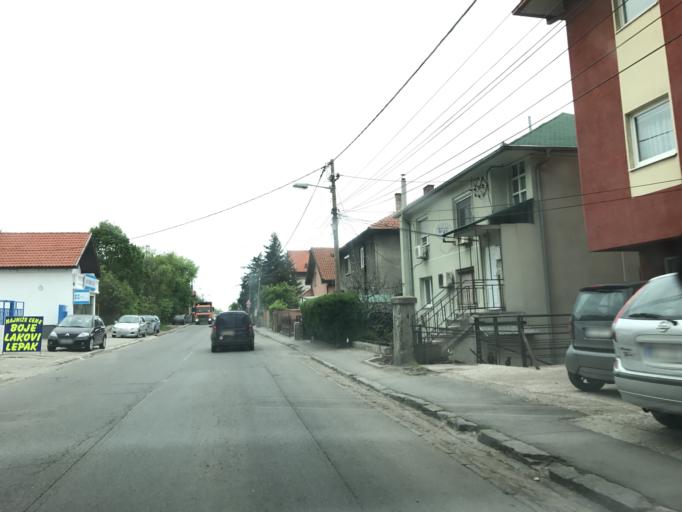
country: RS
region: Central Serbia
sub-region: Belgrade
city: Palilula
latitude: 44.8068
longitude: 20.5158
